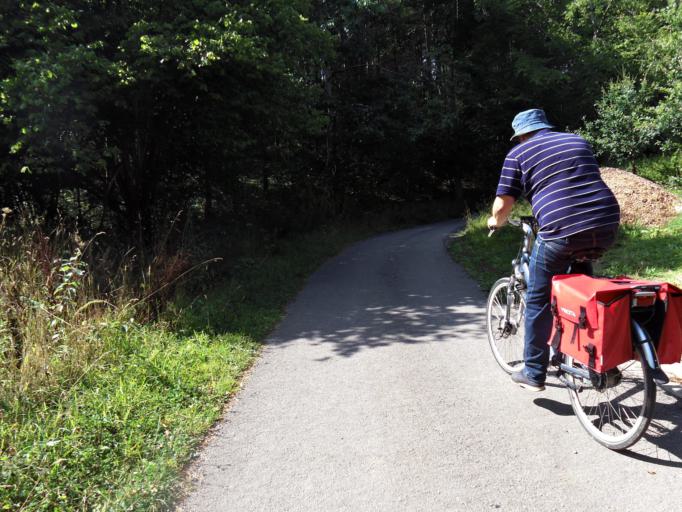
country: BE
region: Wallonia
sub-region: Province de Namur
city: Bievre
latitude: 49.8693
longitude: 4.9930
